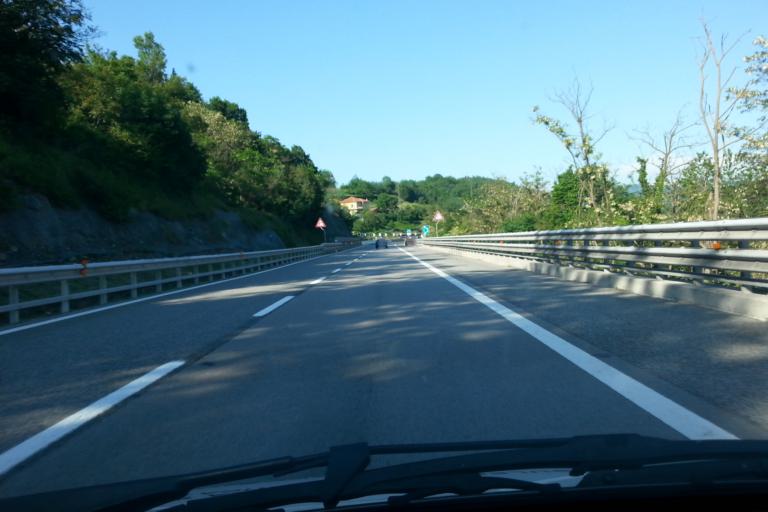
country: IT
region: Liguria
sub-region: Provincia di Savona
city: Cosseria
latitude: 44.3632
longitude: 8.2417
